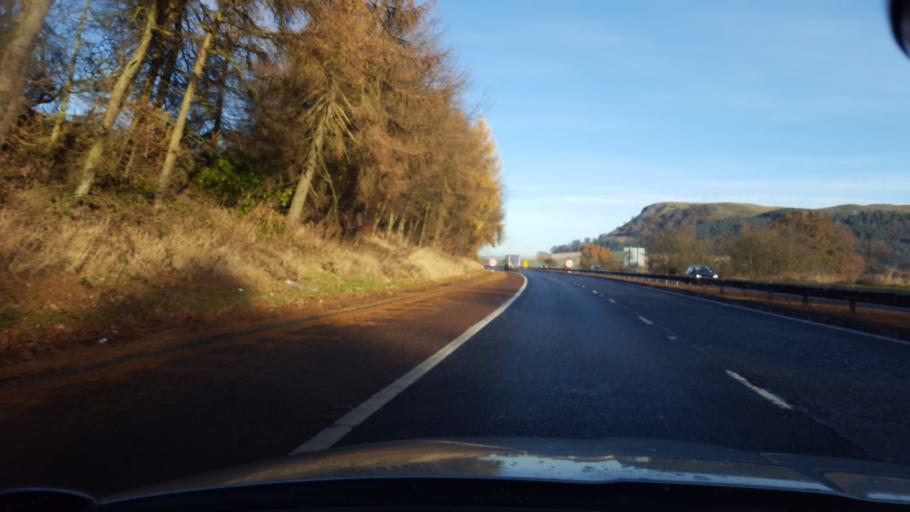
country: GB
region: Scotland
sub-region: Fife
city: Kelty
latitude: 56.1457
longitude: -3.3933
